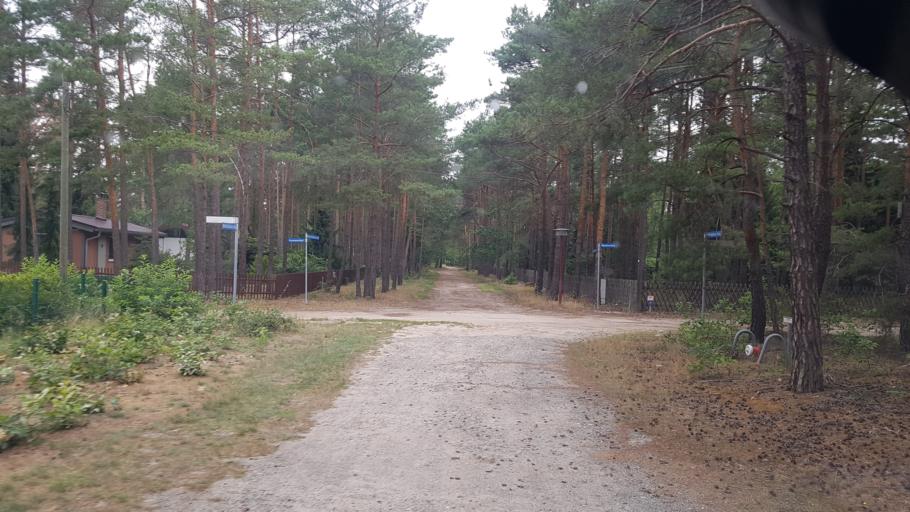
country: DE
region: Brandenburg
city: Gross Koris
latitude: 52.1590
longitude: 13.6990
